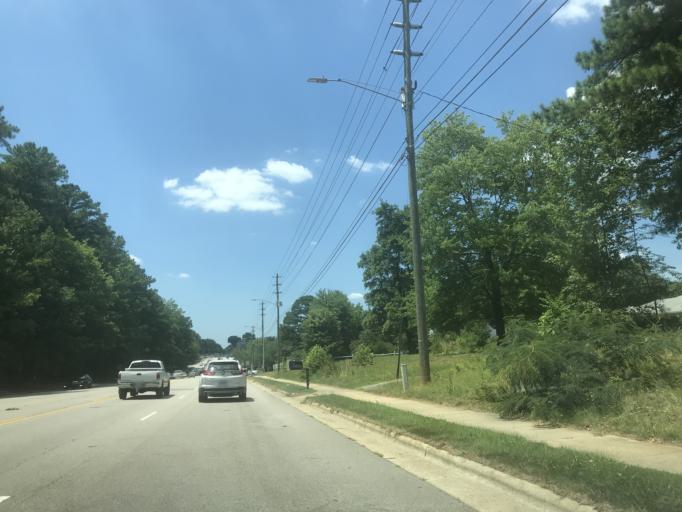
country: US
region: North Carolina
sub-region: Wake County
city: Cary
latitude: 35.7682
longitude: -78.7589
